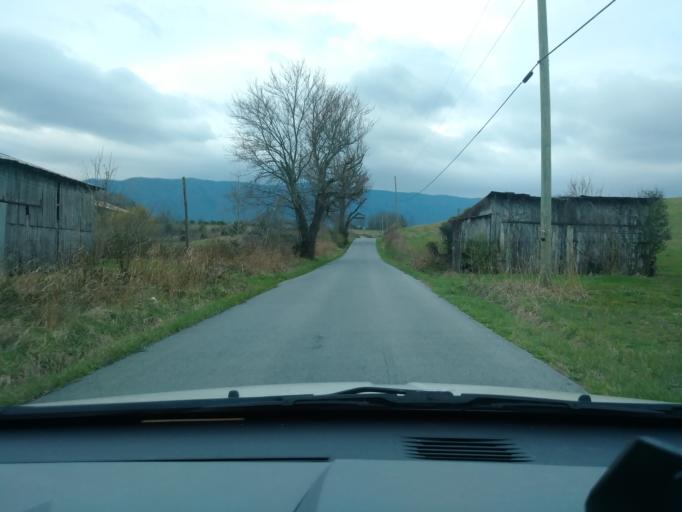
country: US
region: Tennessee
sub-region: Greene County
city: Tusculum
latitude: 36.0945
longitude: -82.7505
